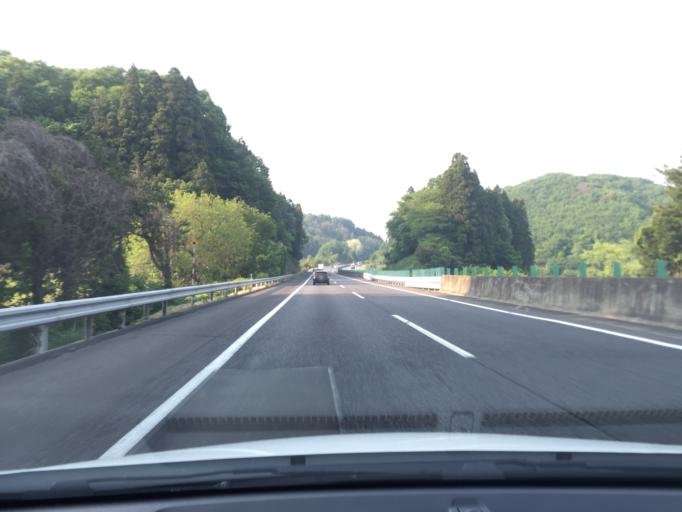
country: JP
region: Fukushima
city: Sukagawa
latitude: 37.1709
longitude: 140.2707
